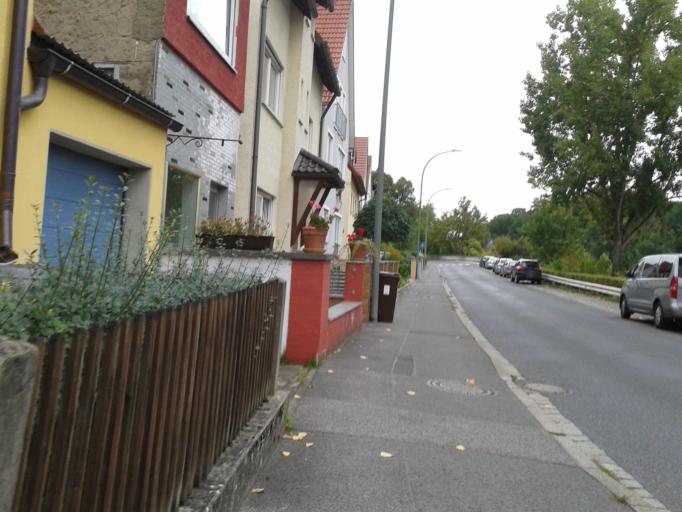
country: DE
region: Bavaria
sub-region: Upper Franconia
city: Bamberg
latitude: 49.8699
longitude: 10.9049
